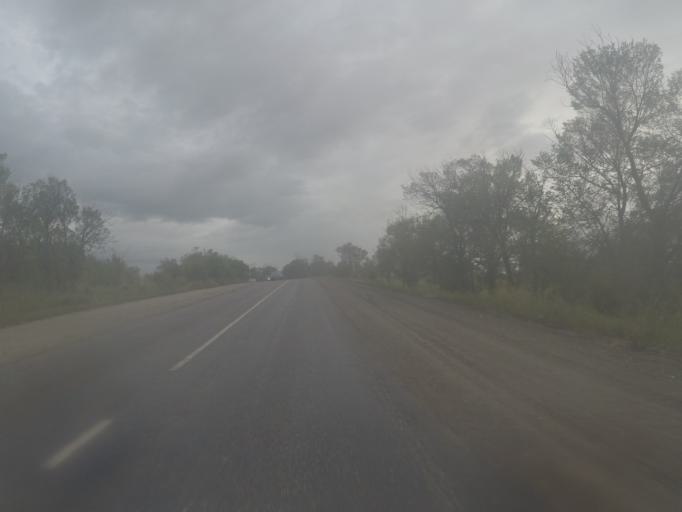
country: KG
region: Ysyk-Koel
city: Tyup
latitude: 42.6718
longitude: 78.3499
